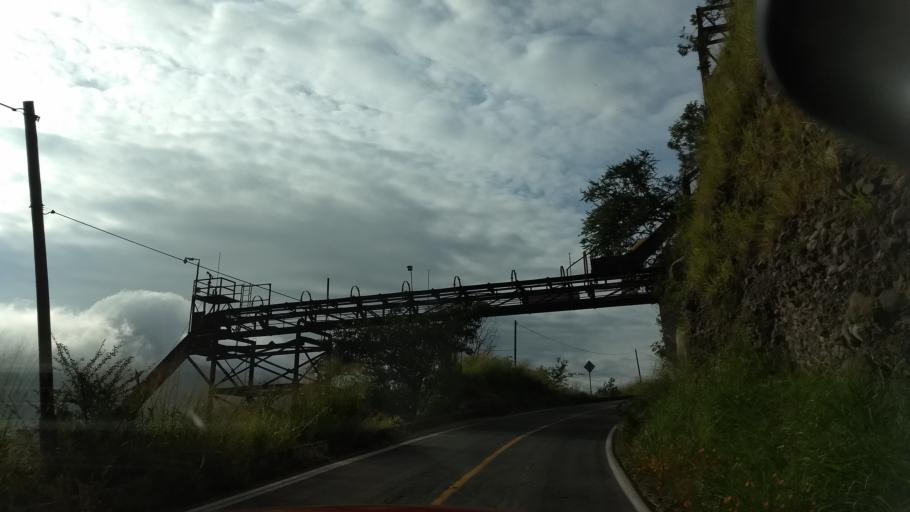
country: MX
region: Jalisco
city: Tuxpan
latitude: 19.5242
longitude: -103.4404
